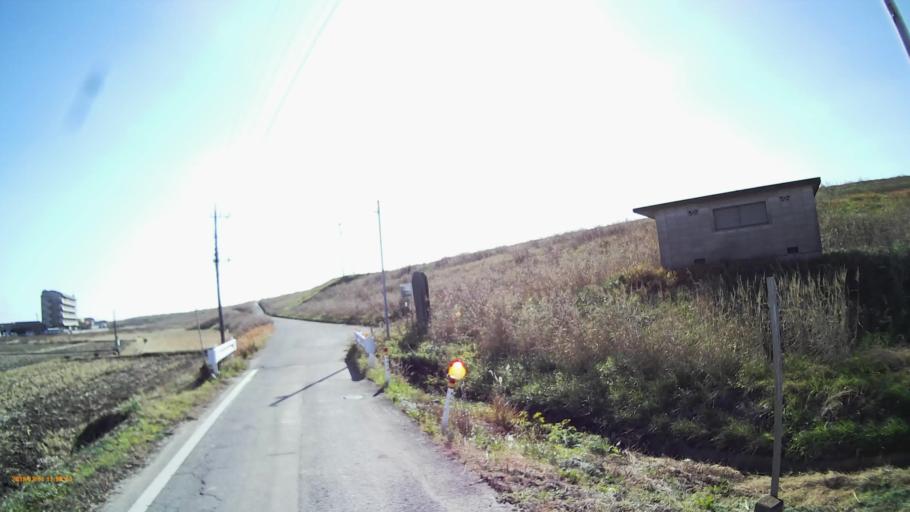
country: JP
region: Saitama
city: Kumagaya
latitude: 36.1191
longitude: 139.4193
